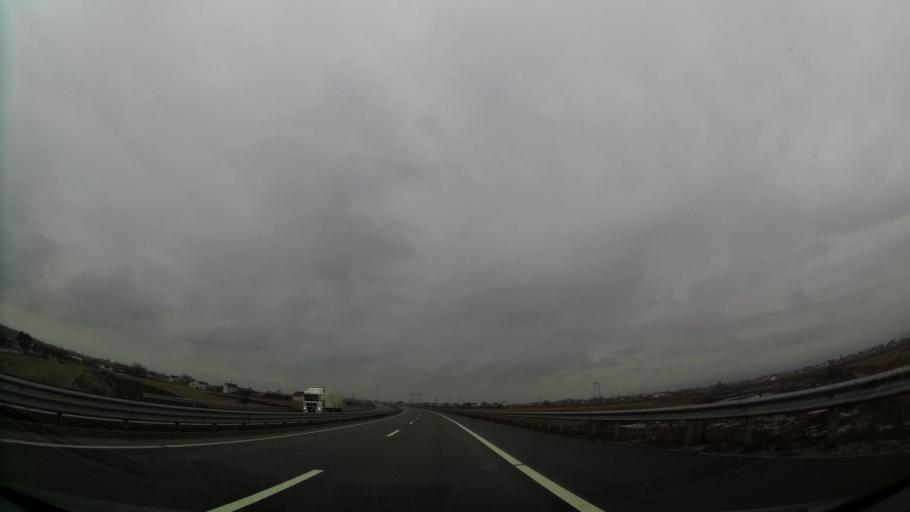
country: XK
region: Ferizaj
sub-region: Komuna e Ferizajt
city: Ferizaj
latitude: 42.4116
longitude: 21.1968
